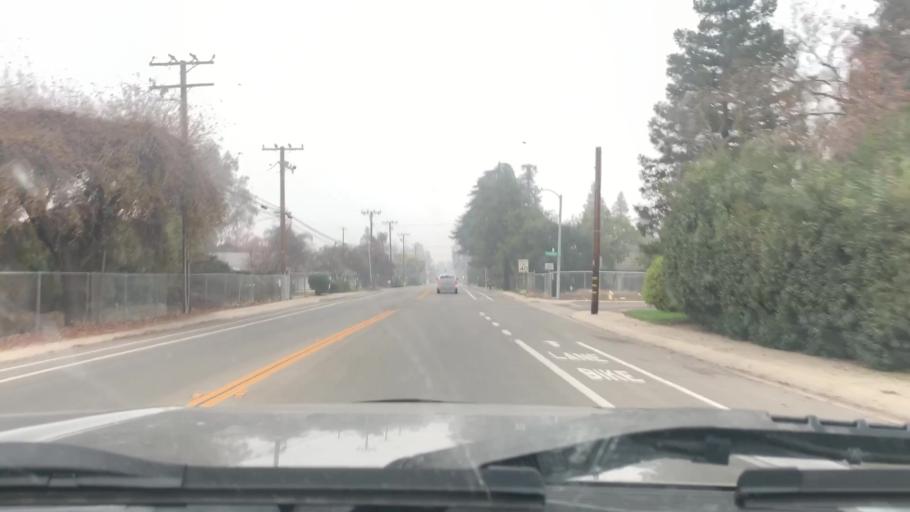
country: US
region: California
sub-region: Tulare County
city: Visalia
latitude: 36.3167
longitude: -119.3054
